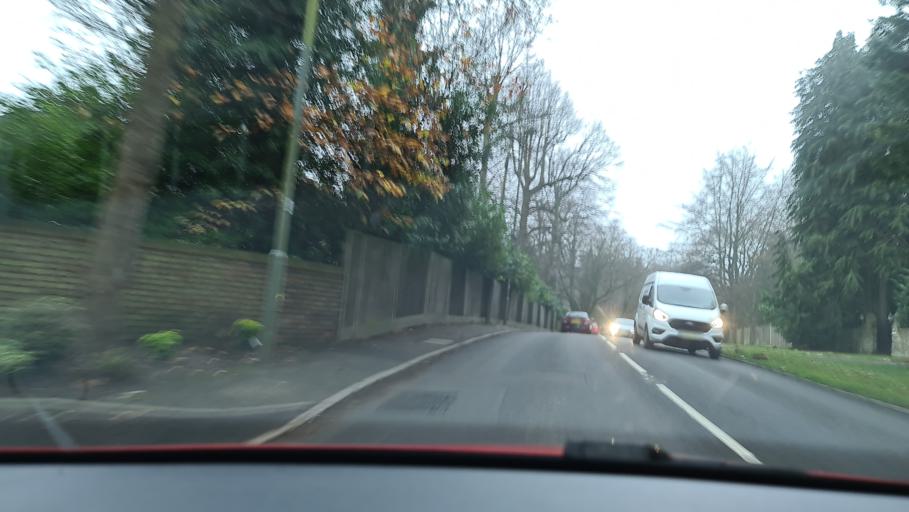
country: GB
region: England
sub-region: Surrey
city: Esher
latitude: 51.3596
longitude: -0.3626
